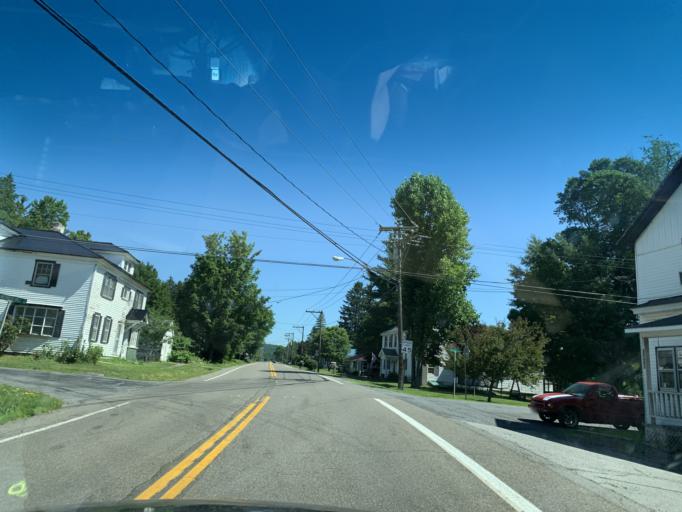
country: US
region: New York
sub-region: Chenango County
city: Norwich
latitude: 42.5126
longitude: -75.4017
